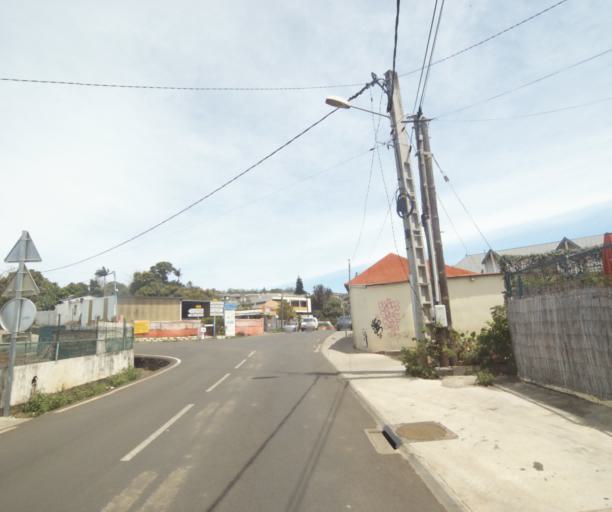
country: RE
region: Reunion
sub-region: Reunion
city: Saint-Paul
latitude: -21.0456
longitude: 55.2858
